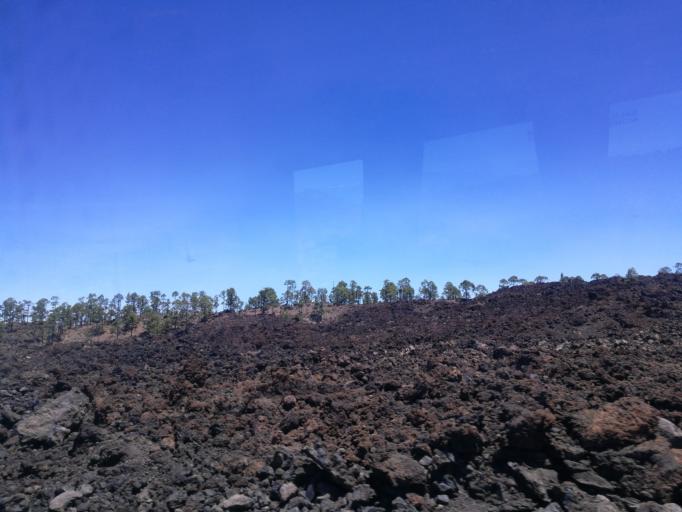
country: ES
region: Canary Islands
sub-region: Provincia de Santa Cruz de Tenerife
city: Guia de Isora
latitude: 28.2758
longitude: -16.7294
